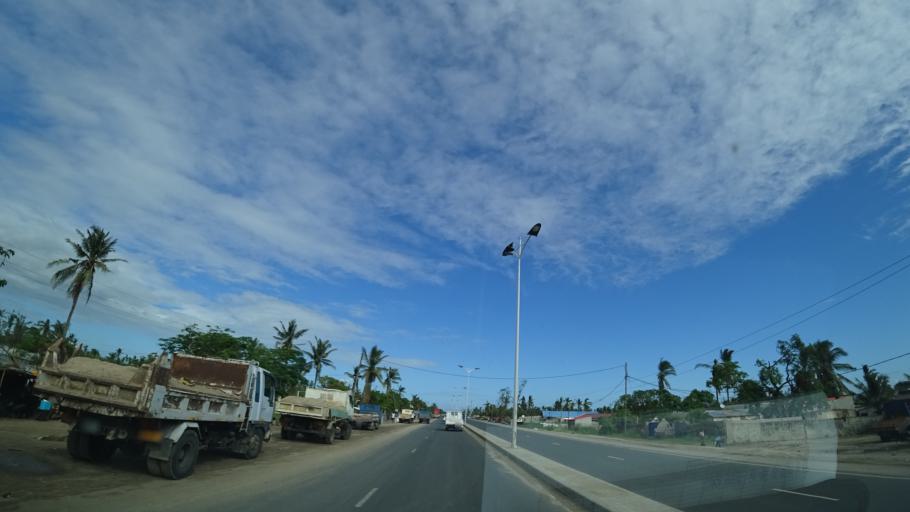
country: MZ
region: Sofala
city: Beira
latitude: -19.7584
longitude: 34.8784
